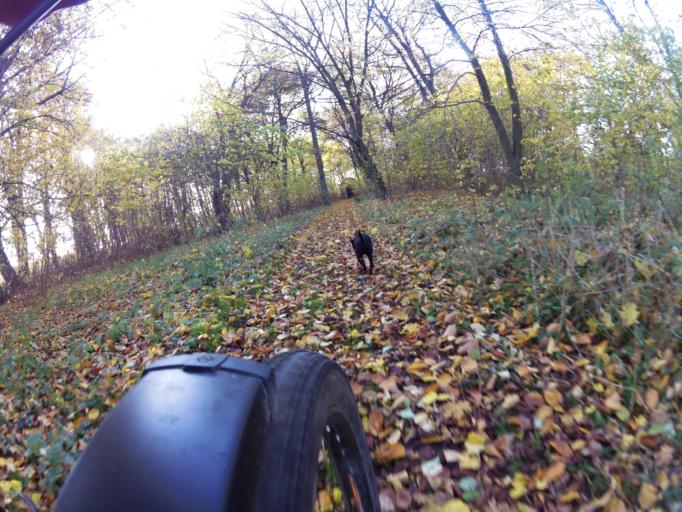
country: PL
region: Pomeranian Voivodeship
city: Strzelno
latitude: 54.7582
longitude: 18.2918
